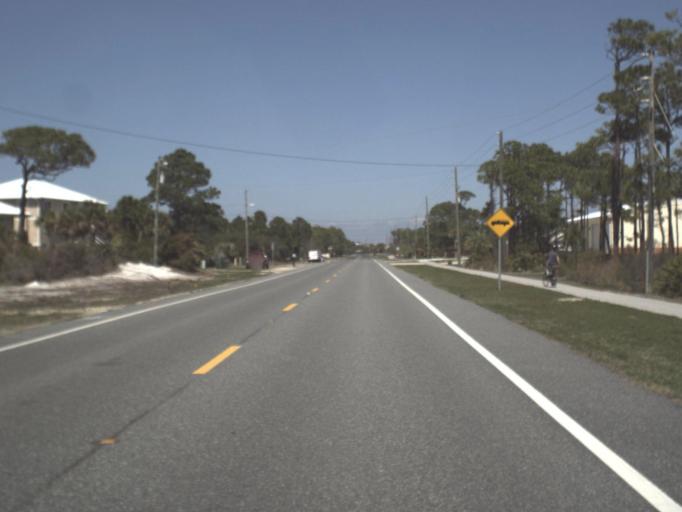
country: US
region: Florida
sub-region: Gulf County
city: Port Saint Joe
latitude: 29.7376
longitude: -85.3935
